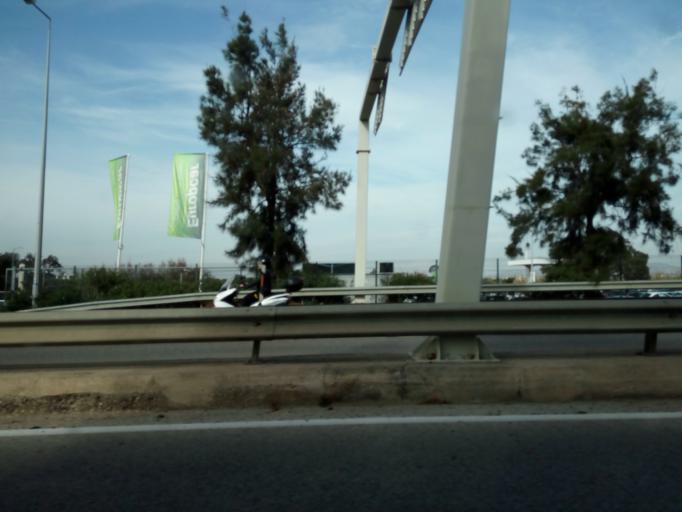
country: PT
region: Faro
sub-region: Faro
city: Faro
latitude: 37.0317
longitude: -7.9668
